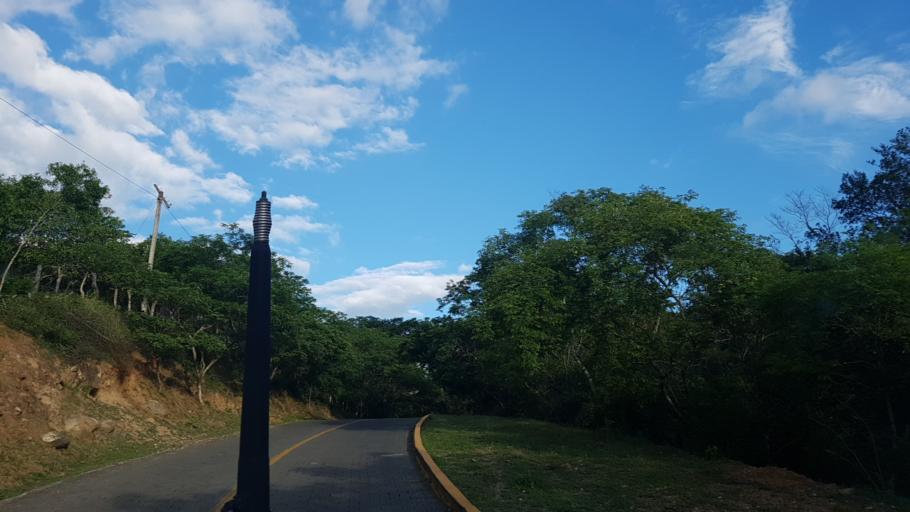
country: NI
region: Nueva Segovia
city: Ocotal
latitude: 13.6421
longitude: -86.5893
